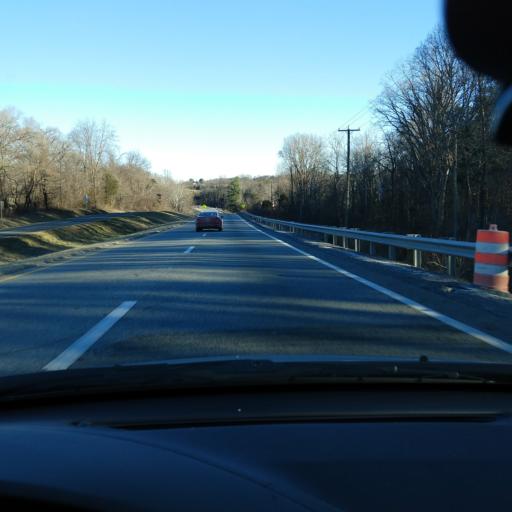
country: US
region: Virginia
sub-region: City of Bedford
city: Bedford
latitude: 37.3527
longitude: -79.6478
